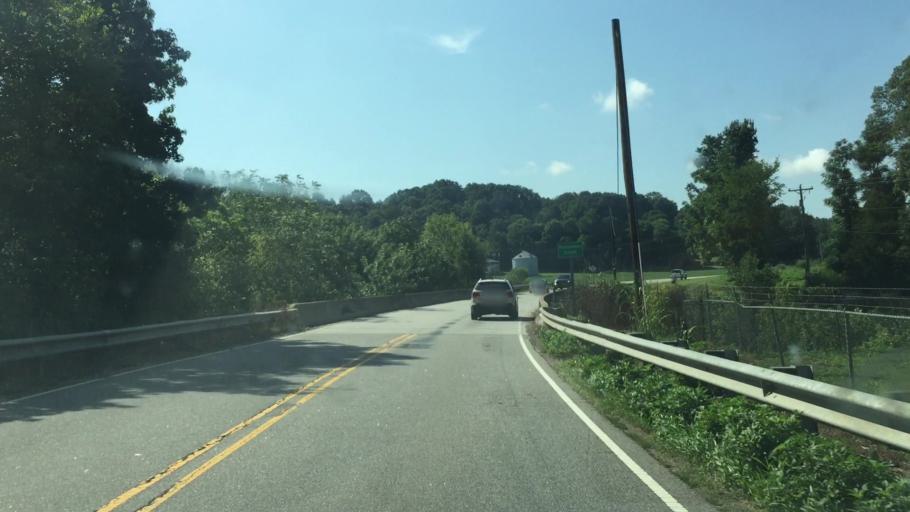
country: US
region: North Carolina
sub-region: Anson County
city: Burnsville
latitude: 35.1151
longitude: -80.3381
